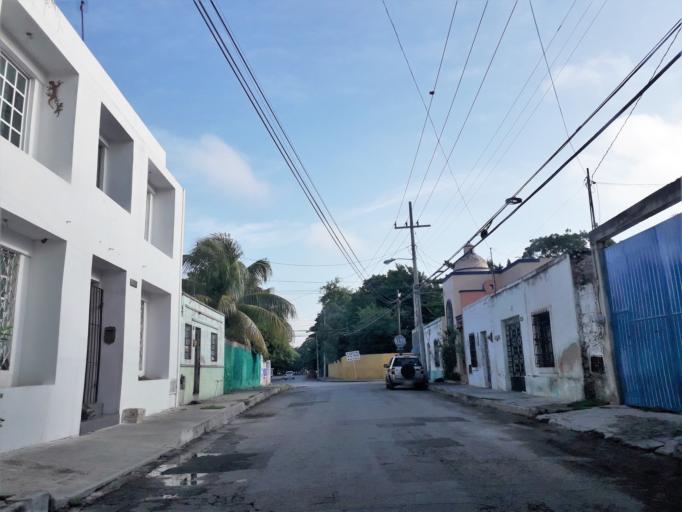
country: MX
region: Yucatan
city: Merida
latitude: 20.9658
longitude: -89.6408
